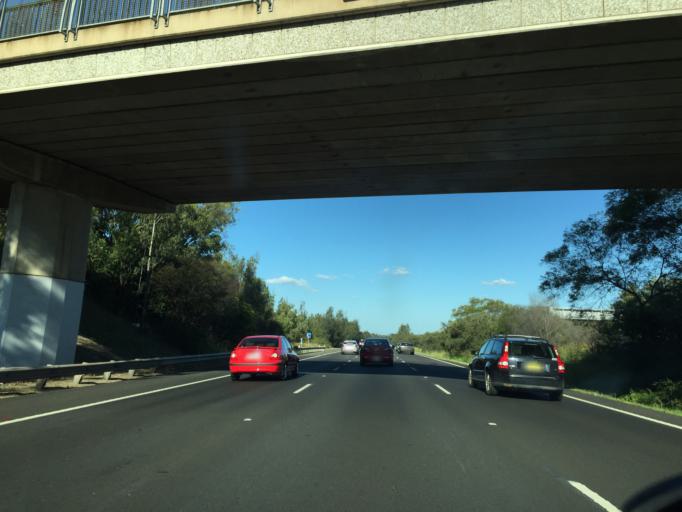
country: AU
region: New South Wales
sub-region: Penrith Municipality
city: Kingswood Park
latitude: -33.7854
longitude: 150.7209
